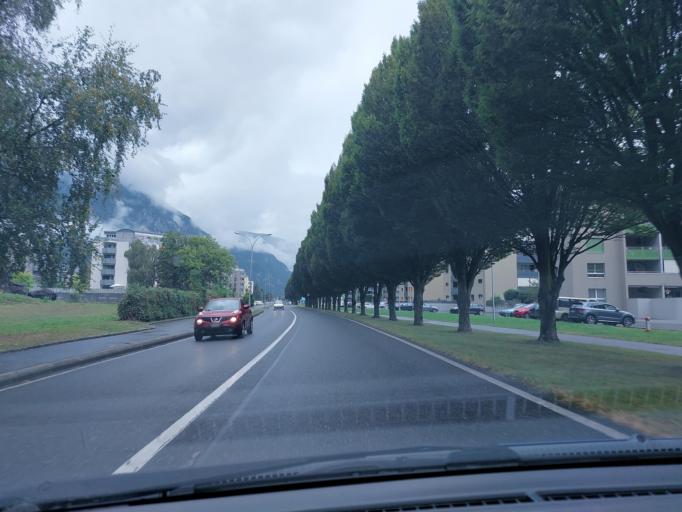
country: CH
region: Valais
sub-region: Monthey District
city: Collombey
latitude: 46.2735
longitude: 6.9434
